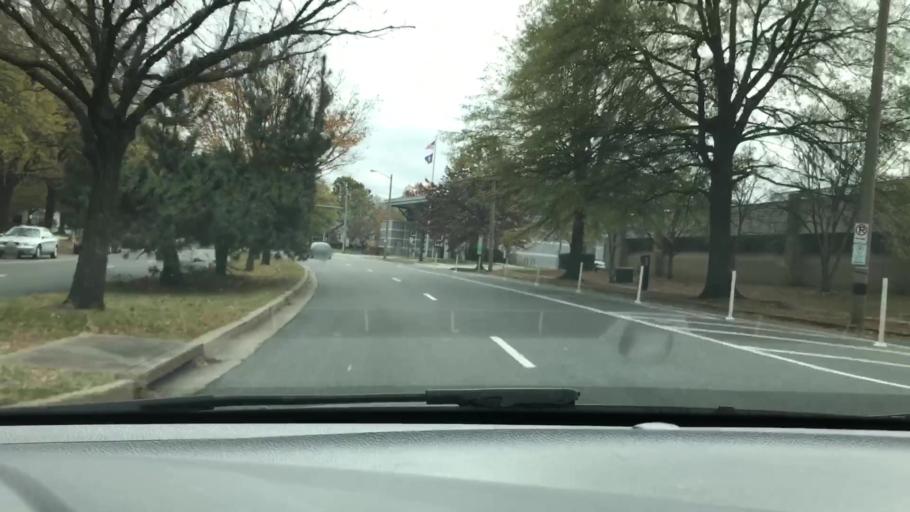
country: US
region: Washington, D.C.
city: Washington, D.C.
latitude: 38.8584
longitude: -77.0590
